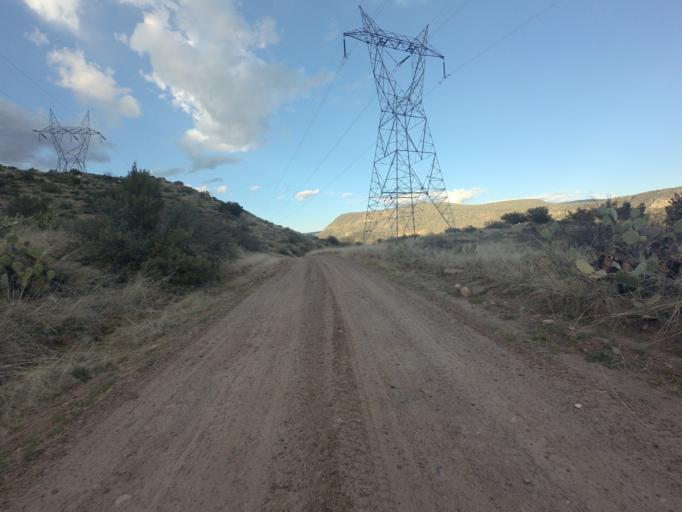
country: US
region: Arizona
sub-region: Gila County
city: Pine
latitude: 34.3660
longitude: -111.6750
